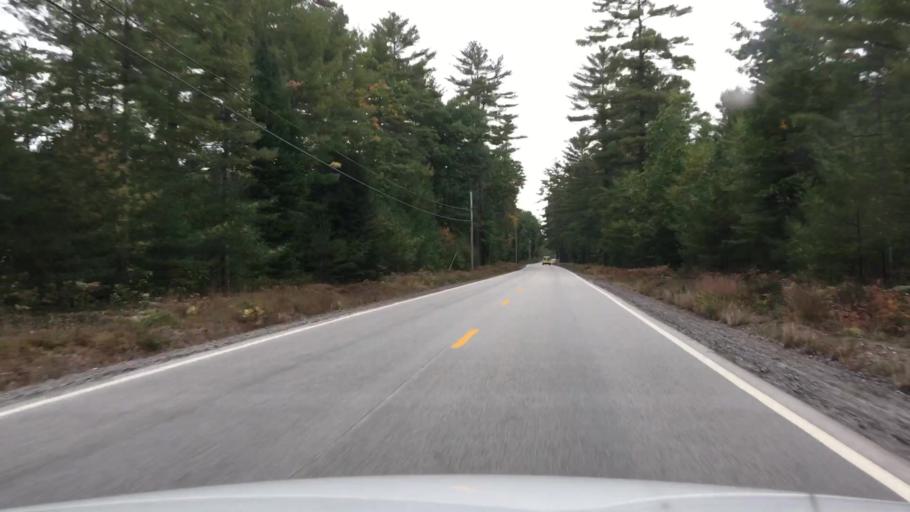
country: US
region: Maine
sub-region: Cumberland County
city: Harrison
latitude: 44.2198
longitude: -70.6907
